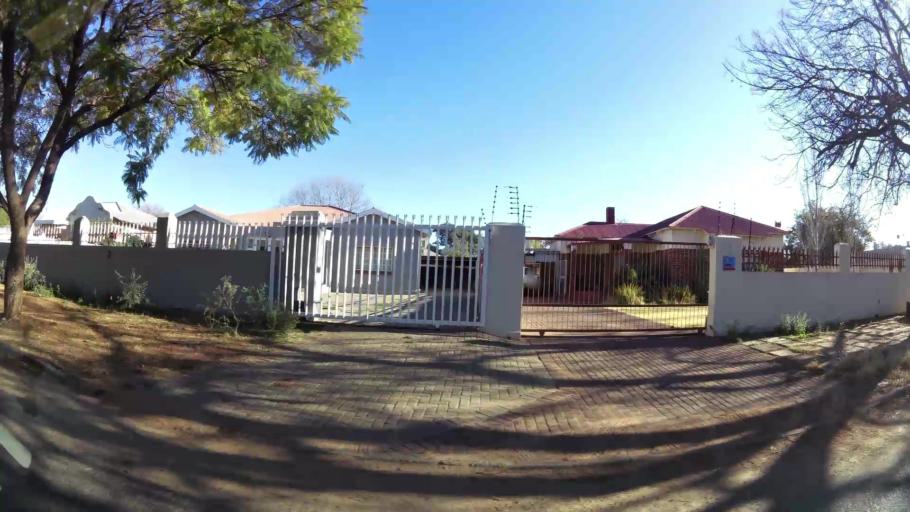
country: ZA
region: Northern Cape
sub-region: Frances Baard District Municipality
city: Kimberley
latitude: -28.7534
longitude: 24.7796
